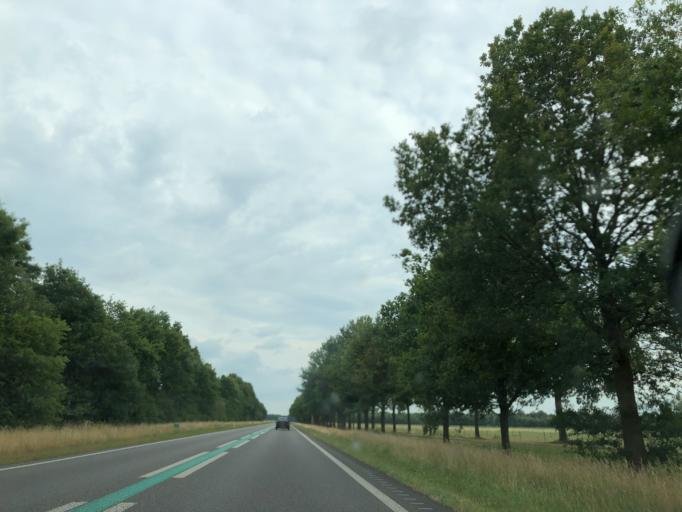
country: NL
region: Drenthe
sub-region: Gemeente Borger-Odoorn
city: Borger
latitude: 52.9866
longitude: 6.7662
